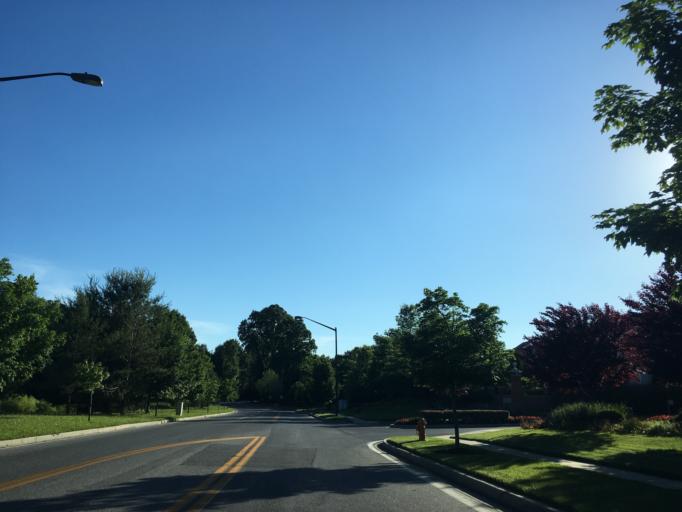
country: US
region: Maryland
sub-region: Howard County
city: Ellicott City
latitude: 39.2930
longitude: -76.8162
